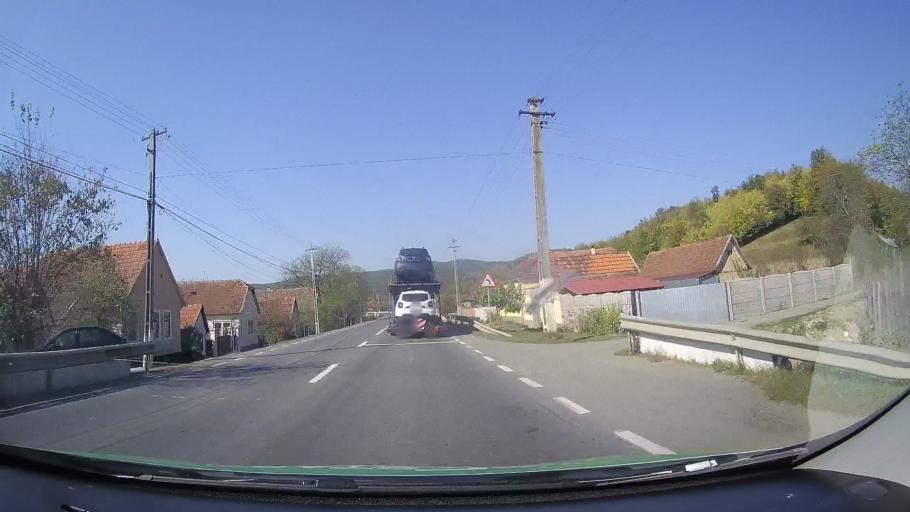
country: RO
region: Arad
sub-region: Comuna Barzava
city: Barzava
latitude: 46.1092
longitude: 21.9801
